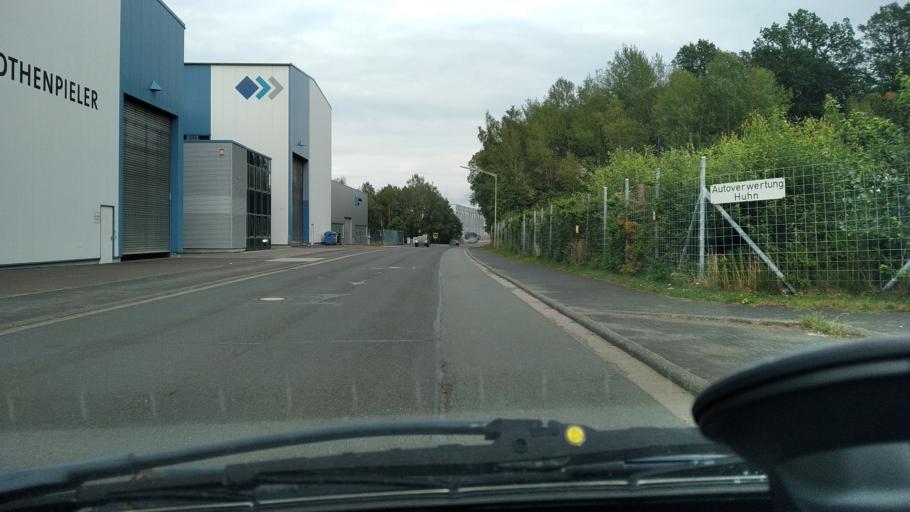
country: DE
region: North Rhine-Westphalia
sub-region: Regierungsbezirk Arnsberg
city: Burbach
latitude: 50.7540
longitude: 8.1127
